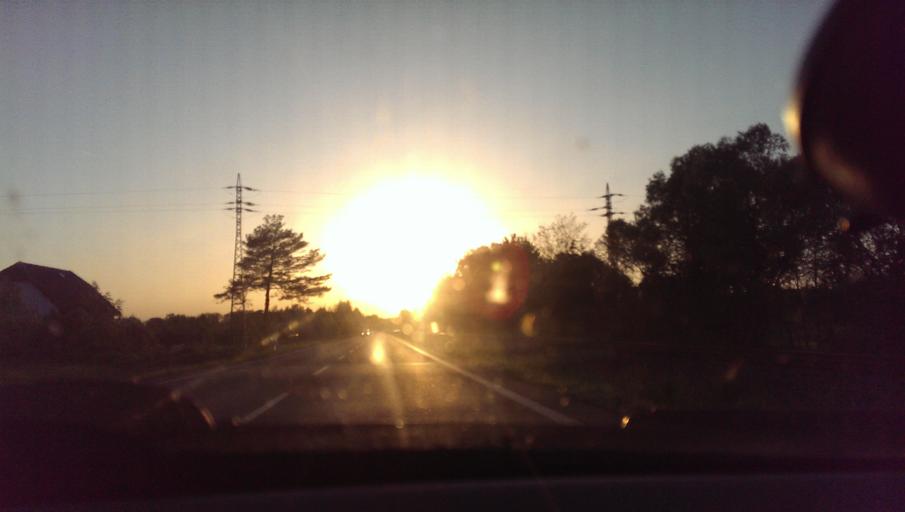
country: CZ
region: Zlin
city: Zasova
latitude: 49.4691
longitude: 18.0354
